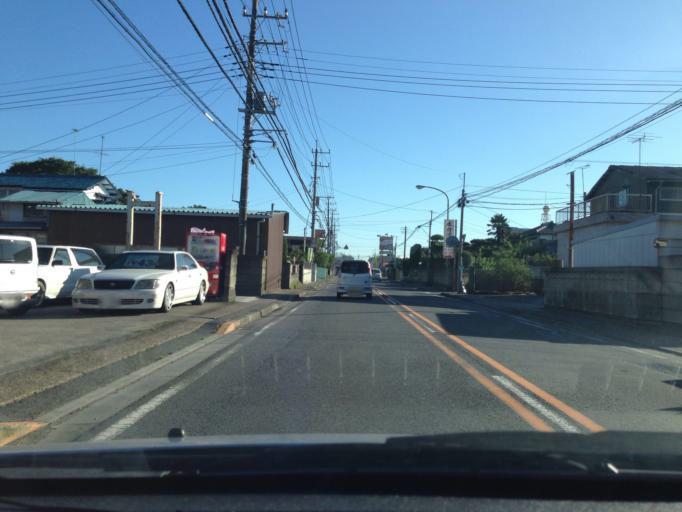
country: JP
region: Ibaraki
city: Naka
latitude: 36.0709
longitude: 140.1873
